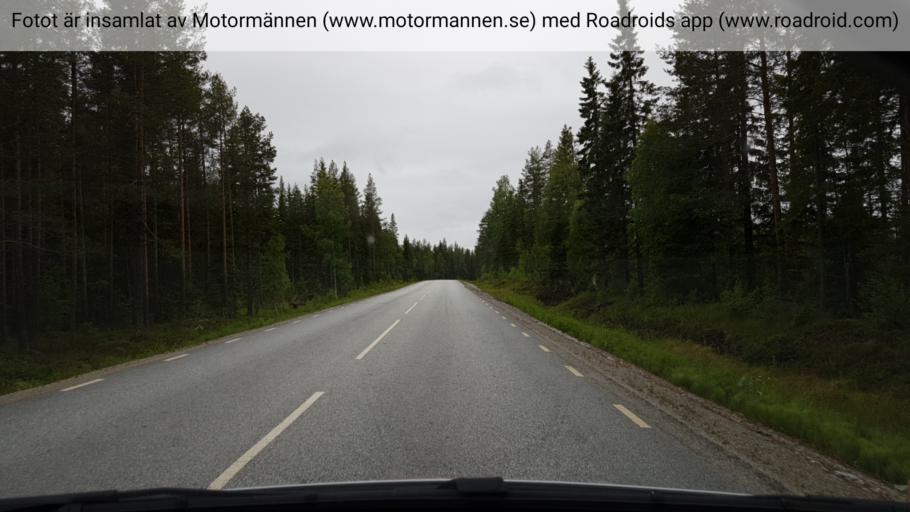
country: SE
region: Vaesterbotten
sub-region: Bjurholms Kommun
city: Bjurholm
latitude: 64.1754
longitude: 19.4005
